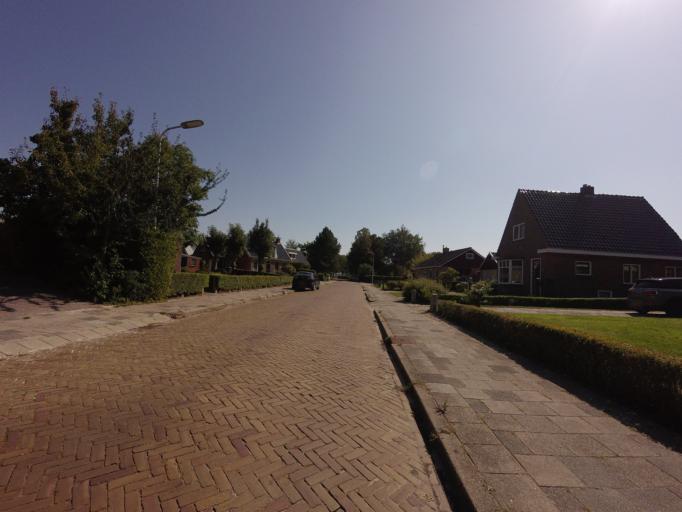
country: NL
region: Friesland
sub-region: Gemeente Dongeradeel
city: Holwerd
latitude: 53.3674
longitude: 5.9049
